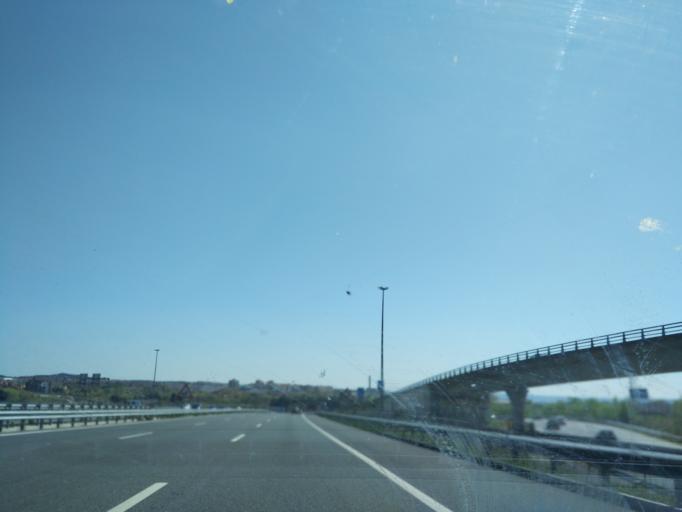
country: ES
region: Madrid
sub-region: Provincia de Madrid
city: Villa de Vallecas
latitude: 40.3594
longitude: -3.5622
